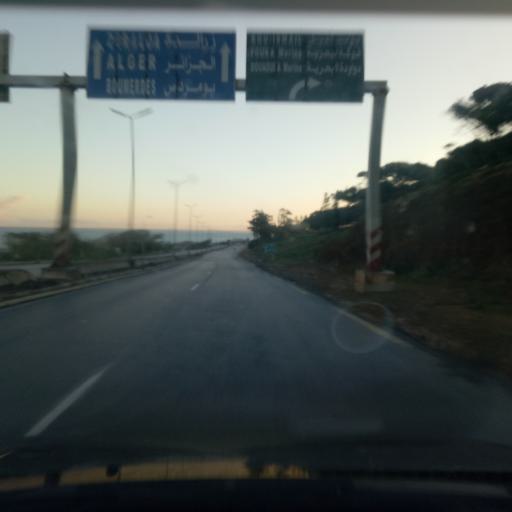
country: DZ
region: Tipaza
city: Bou Ismail
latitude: 36.6562
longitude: 2.7196
